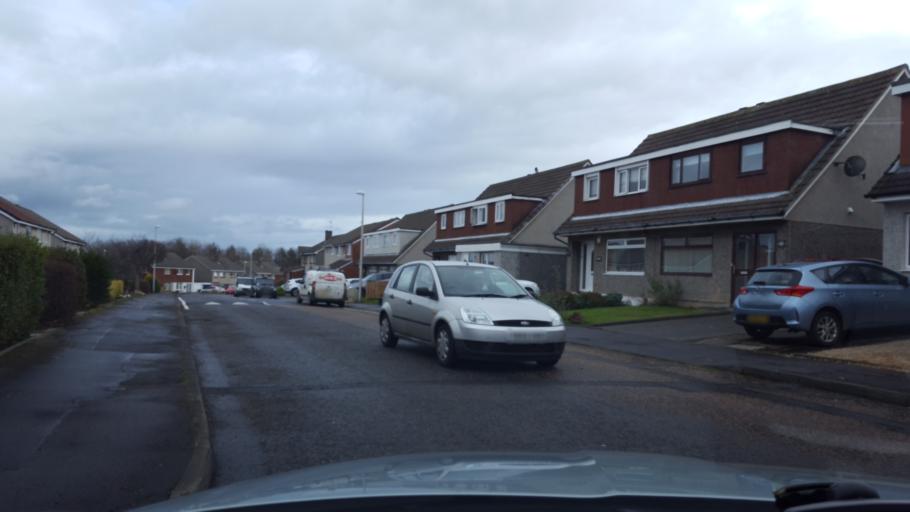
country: GB
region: Scotland
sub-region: Edinburgh
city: Currie
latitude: 55.9106
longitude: -3.2896
